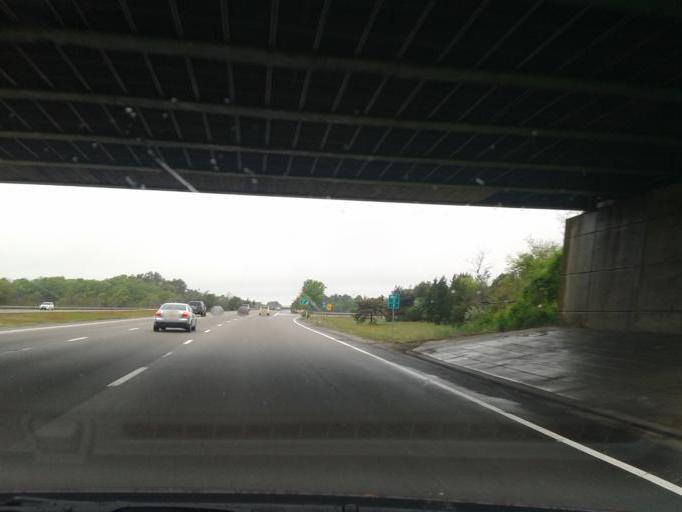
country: US
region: Massachusetts
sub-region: Plymouth County
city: Onset
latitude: 41.7650
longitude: -70.6712
